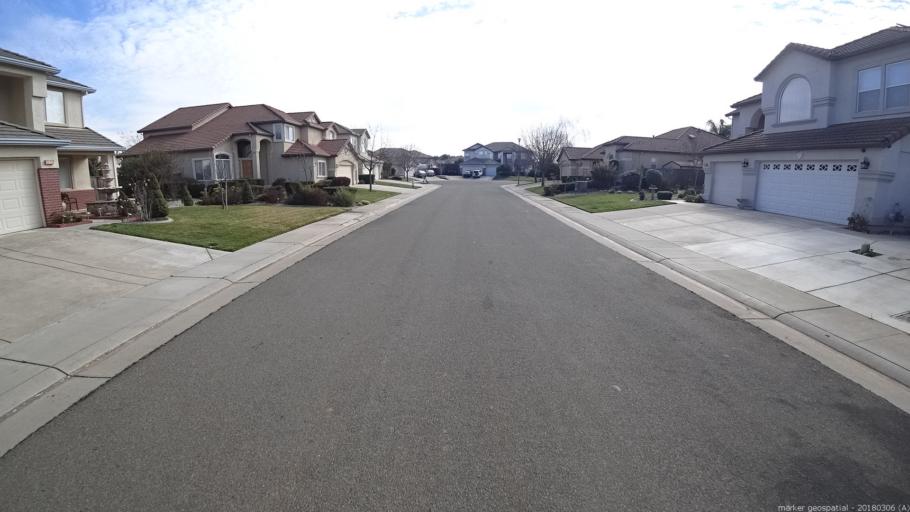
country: US
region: California
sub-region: Sacramento County
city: Vineyard
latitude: 38.4724
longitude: -121.3102
